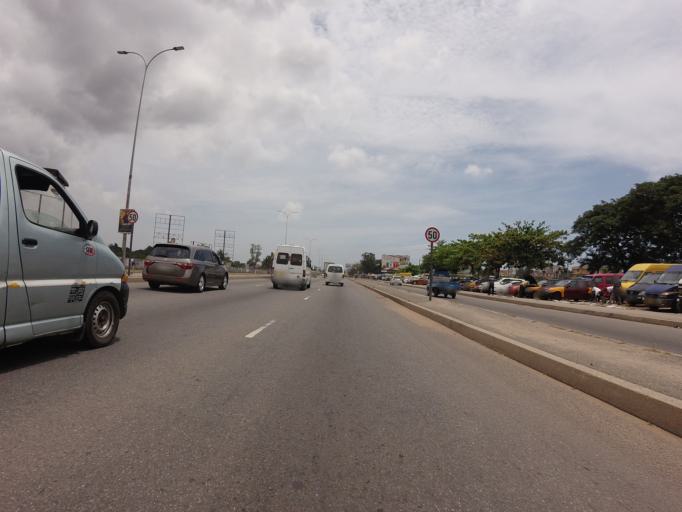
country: GH
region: Greater Accra
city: Accra
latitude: 5.5715
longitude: -0.2465
